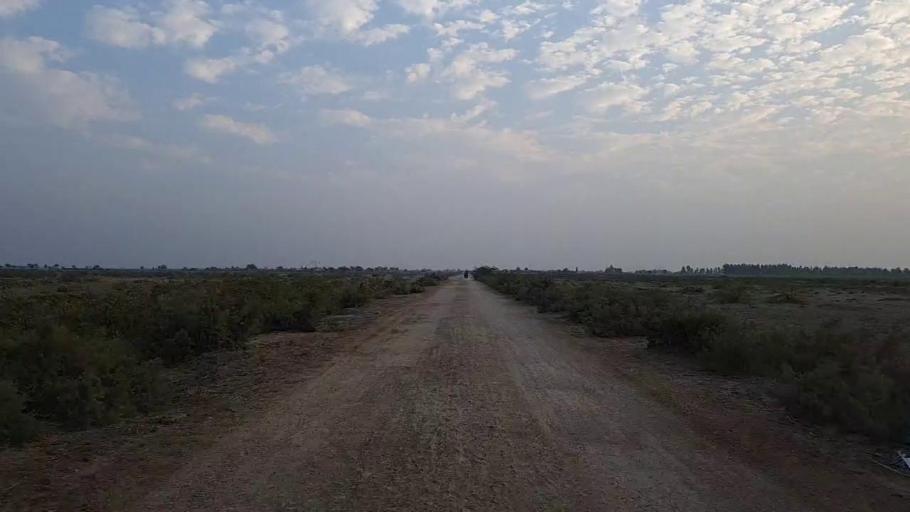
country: PK
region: Sindh
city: Pithoro
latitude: 25.4506
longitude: 69.3451
